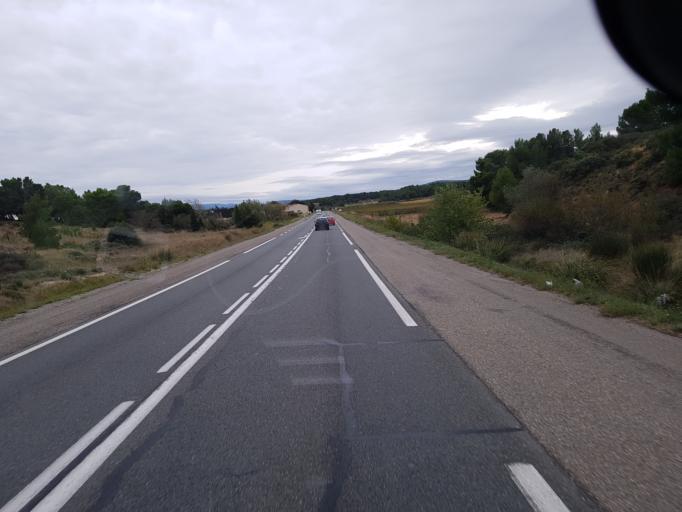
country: FR
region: Languedoc-Roussillon
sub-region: Departement de l'Aude
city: Peyriac-de-Mer
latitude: 43.1260
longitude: 2.9585
